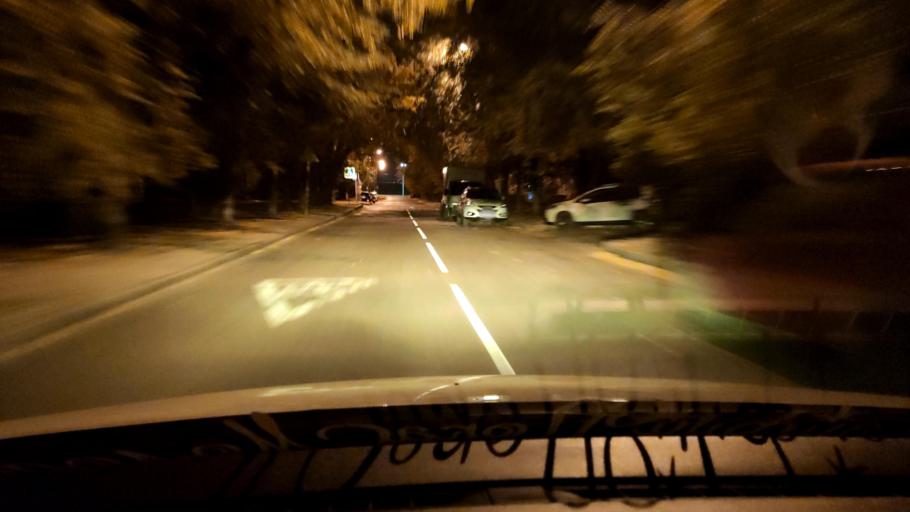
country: RU
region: Voronezj
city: Voronezh
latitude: 51.6497
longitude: 39.1705
